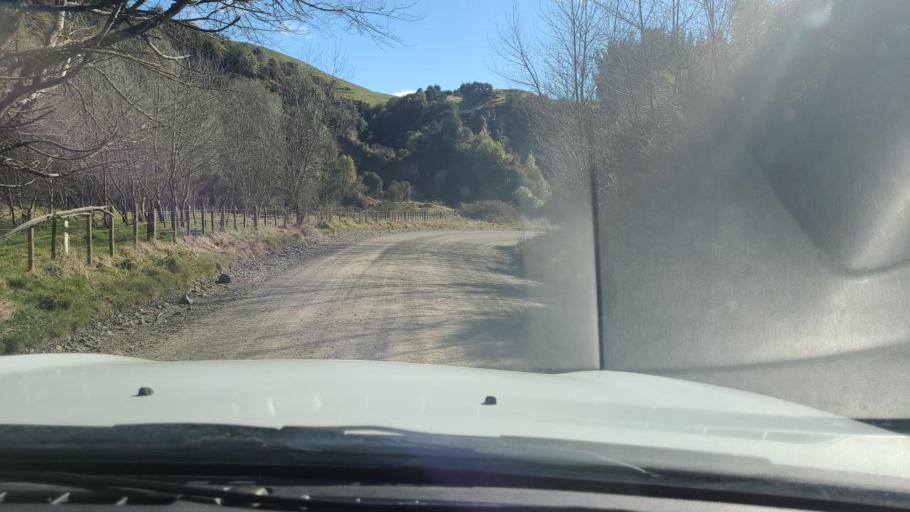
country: NZ
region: Hawke's Bay
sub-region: Napier City
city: Taradale
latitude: -39.2131
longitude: 176.5098
